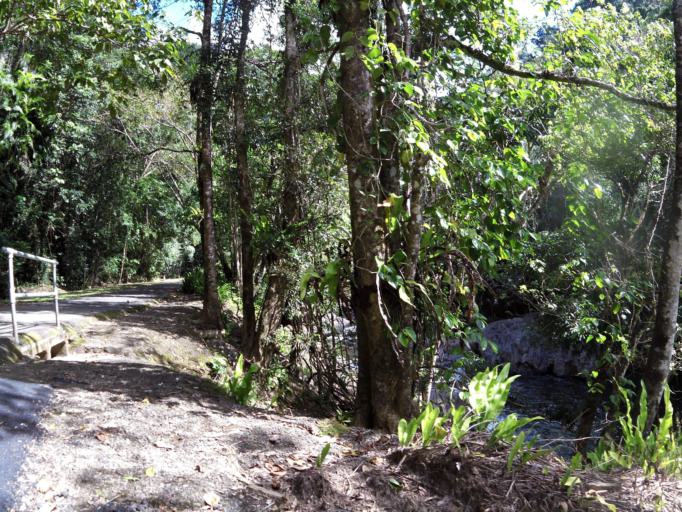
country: AU
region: Queensland
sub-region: Cairns
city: Woree
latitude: -16.9646
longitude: 145.6764
